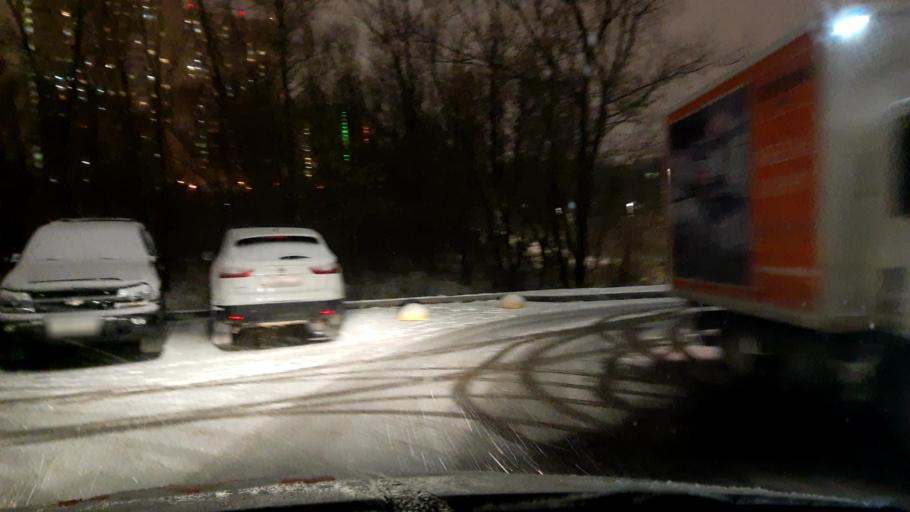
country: RU
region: Moscow
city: Nikulino
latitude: 55.6830
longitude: 37.4626
